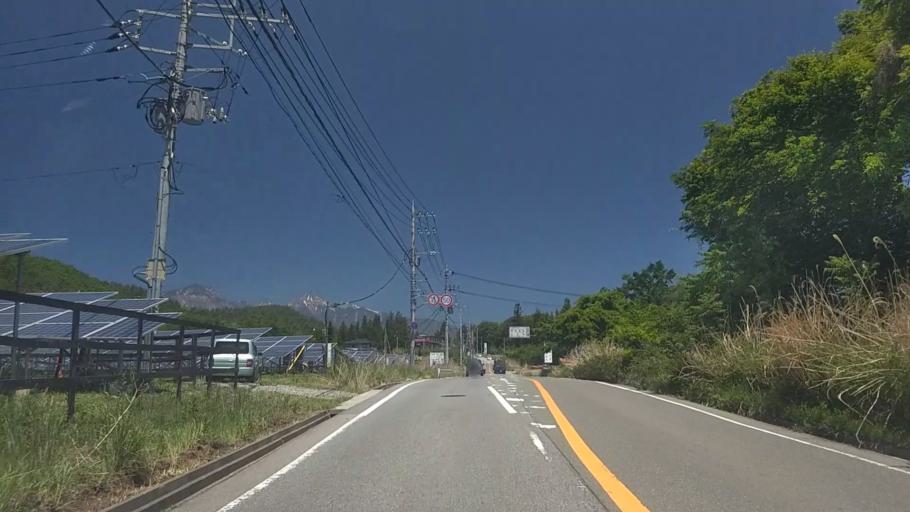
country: JP
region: Yamanashi
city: Nirasaki
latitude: 35.8508
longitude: 138.4321
